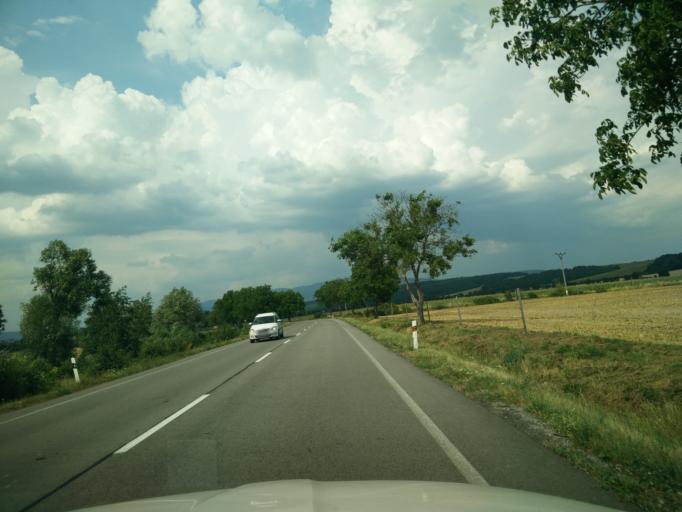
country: SK
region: Nitriansky
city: Novaky
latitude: 48.7370
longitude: 18.5017
